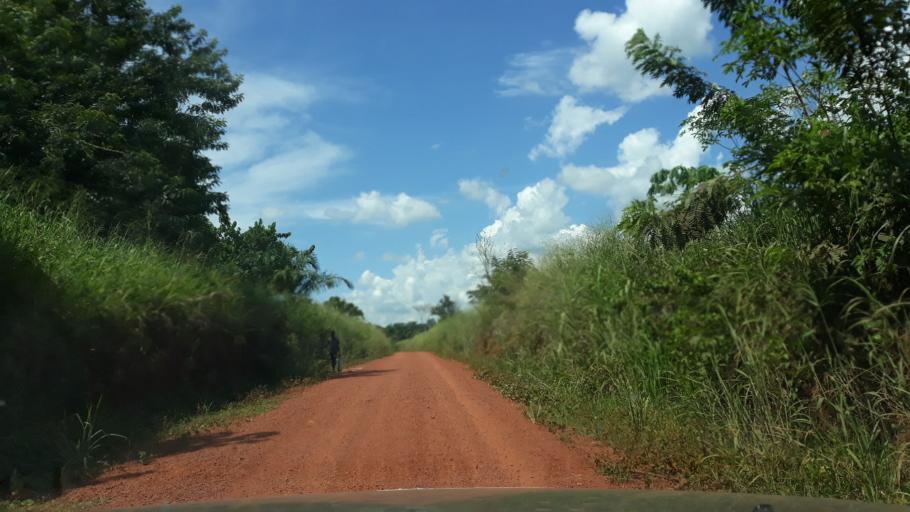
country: CD
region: Equateur
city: Businga
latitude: 3.4050
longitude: 20.3889
